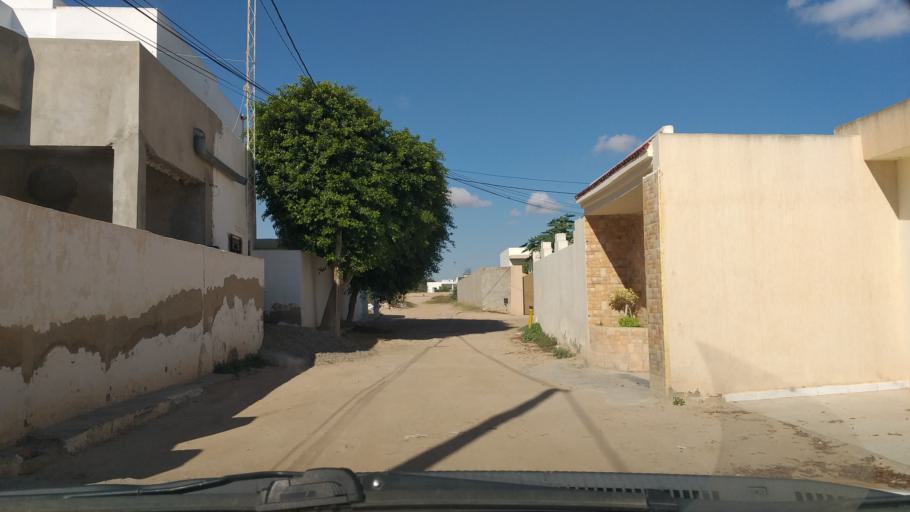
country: TN
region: Safaqis
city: Al Qarmadah
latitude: 34.8017
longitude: 10.7690
